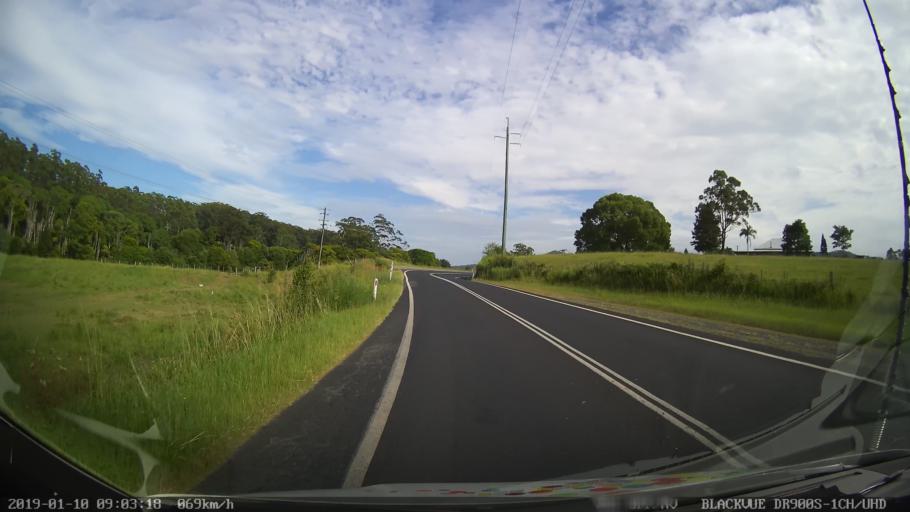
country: AU
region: New South Wales
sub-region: Coffs Harbour
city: Coffs Harbour
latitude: -30.2652
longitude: 153.0482
